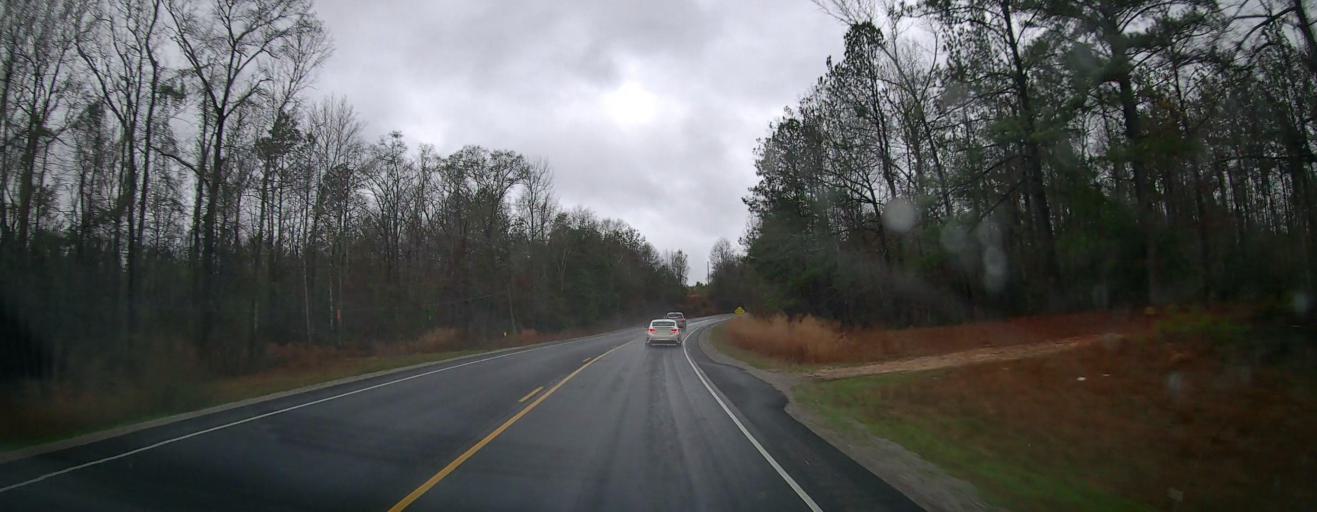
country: US
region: Alabama
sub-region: Chilton County
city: Clanton
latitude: 32.6186
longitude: -86.7334
